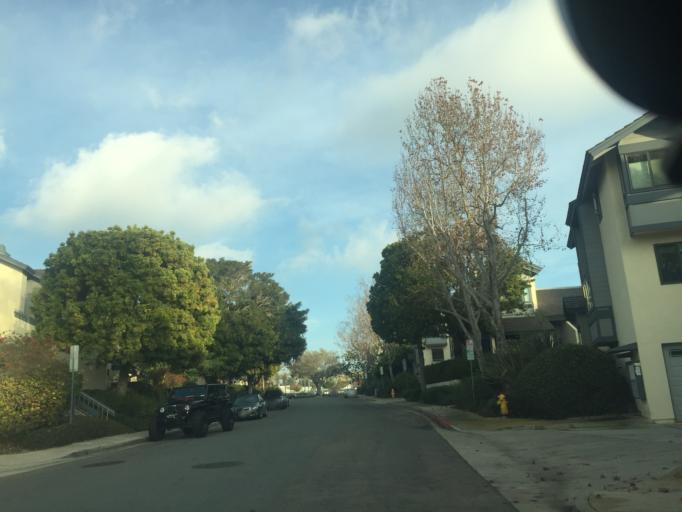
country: US
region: California
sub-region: San Diego County
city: La Jolla
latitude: 32.8686
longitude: -117.2352
